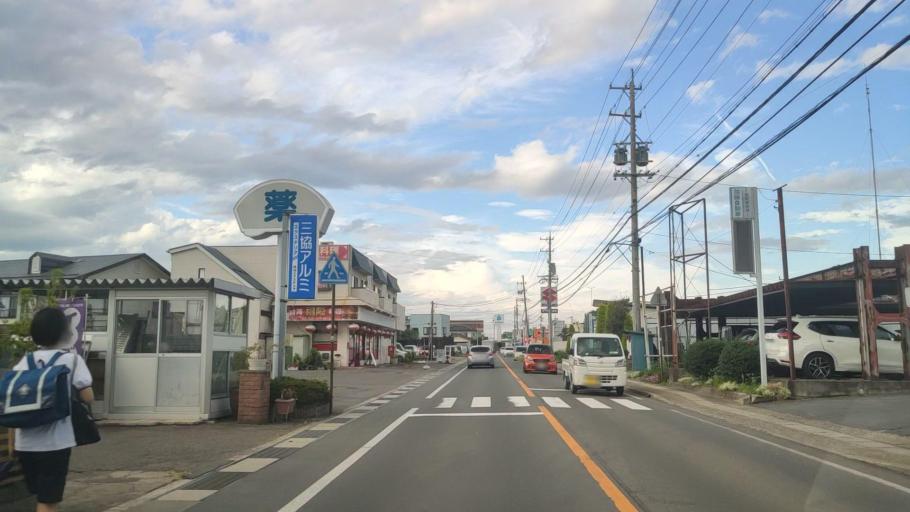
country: JP
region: Nagano
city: Suzaka
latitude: 36.6689
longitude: 138.3158
